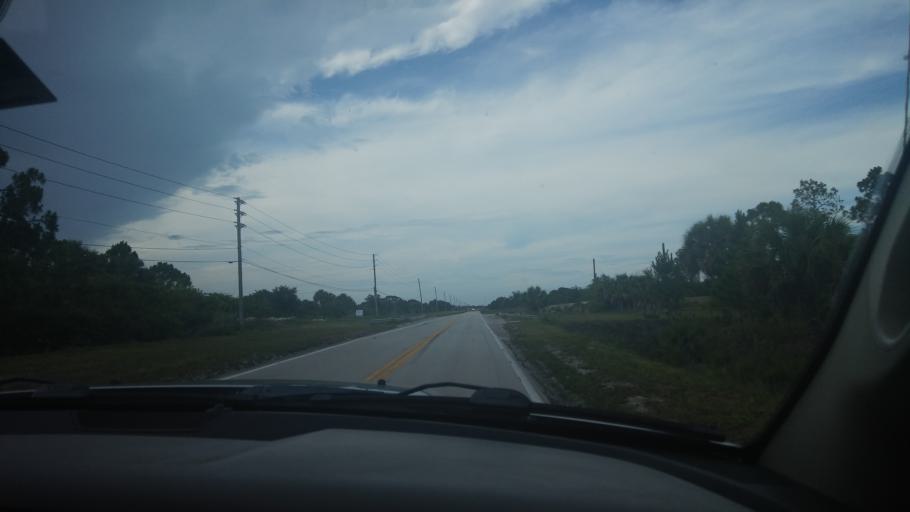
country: US
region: Florida
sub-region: Brevard County
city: Grant-Valkaria
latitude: 27.8878
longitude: -80.6224
